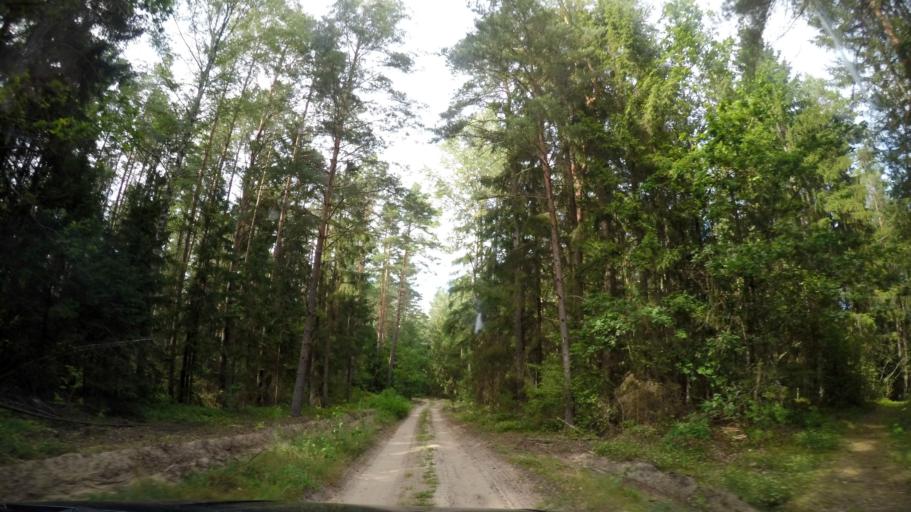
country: BY
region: Grodnenskaya
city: Skidal'
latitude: 53.8390
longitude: 24.1764
